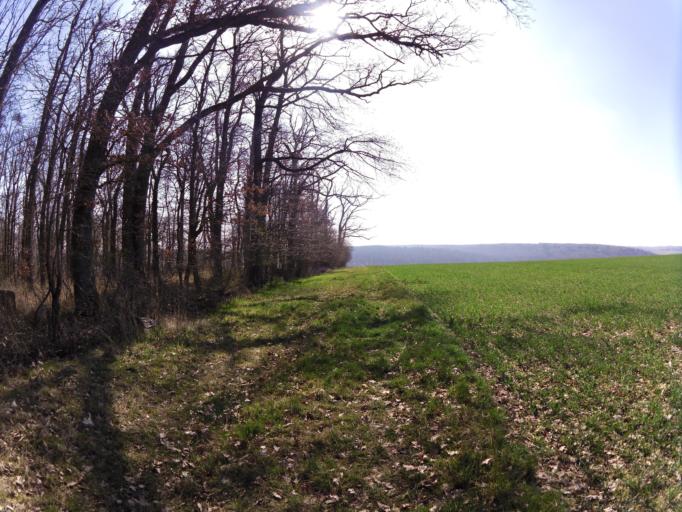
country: DE
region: Bavaria
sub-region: Regierungsbezirk Unterfranken
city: Greussenheim
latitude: 49.8040
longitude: 9.7849
